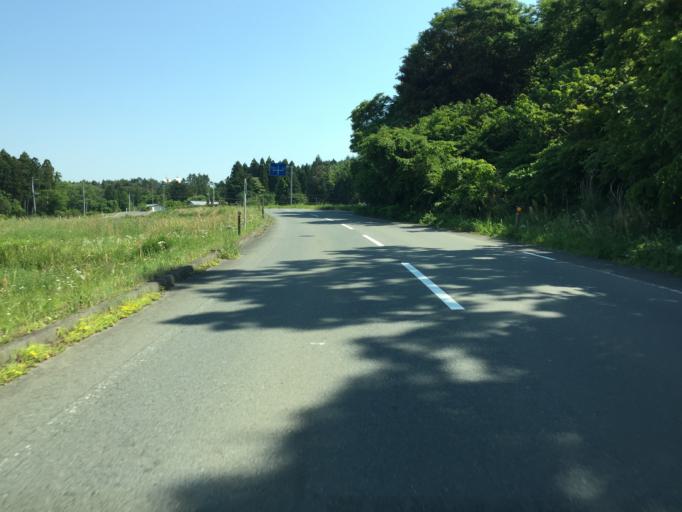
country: JP
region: Miyagi
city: Marumori
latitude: 37.8001
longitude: 140.8814
